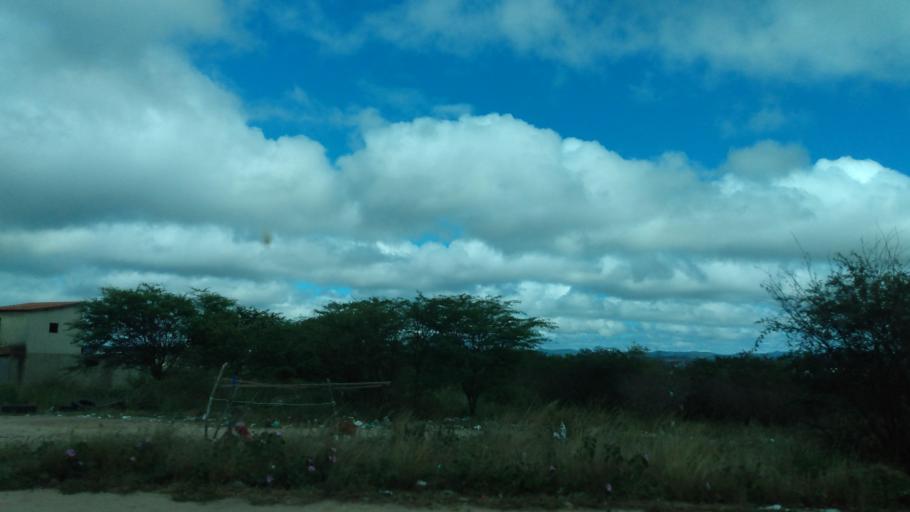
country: BR
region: Pernambuco
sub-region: Caruaru
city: Caruaru
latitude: -8.3114
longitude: -35.9907
